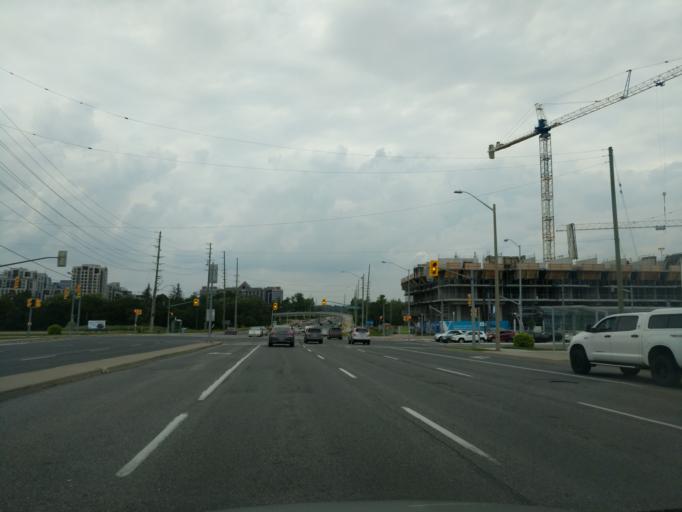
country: CA
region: Ontario
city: Markham
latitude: 43.8479
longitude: -79.3317
